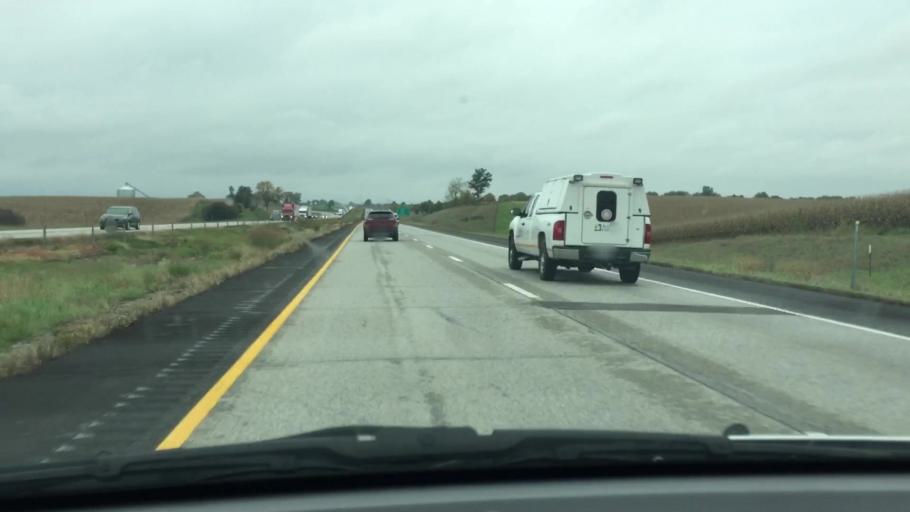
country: US
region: Iowa
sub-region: Johnson County
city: Tiffin
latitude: 41.6877
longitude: -91.7901
